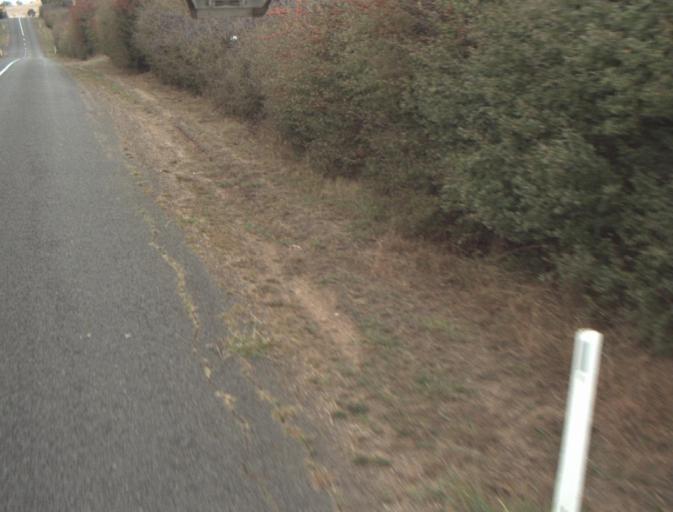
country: AU
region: Tasmania
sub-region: Northern Midlands
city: Evandale
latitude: -41.5183
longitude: 147.2180
